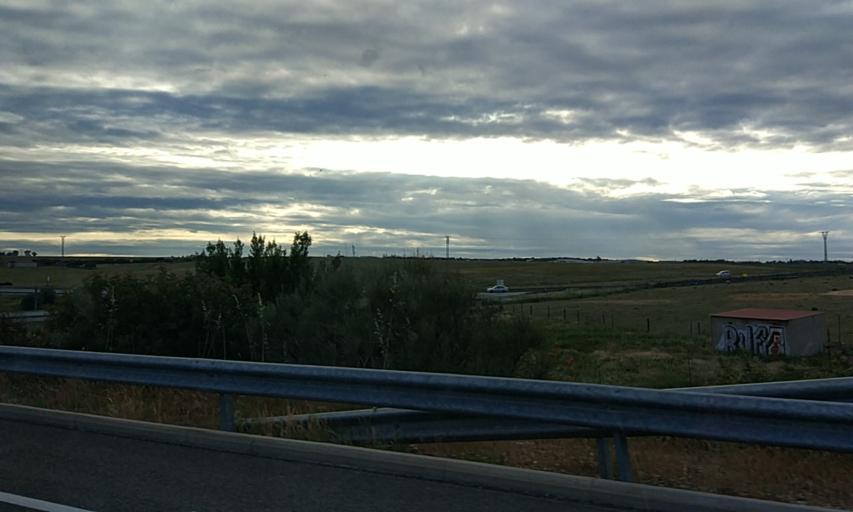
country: ES
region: Extremadura
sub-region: Provincia de Caceres
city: Casar de Caceres
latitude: 39.5384
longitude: -6.4066
